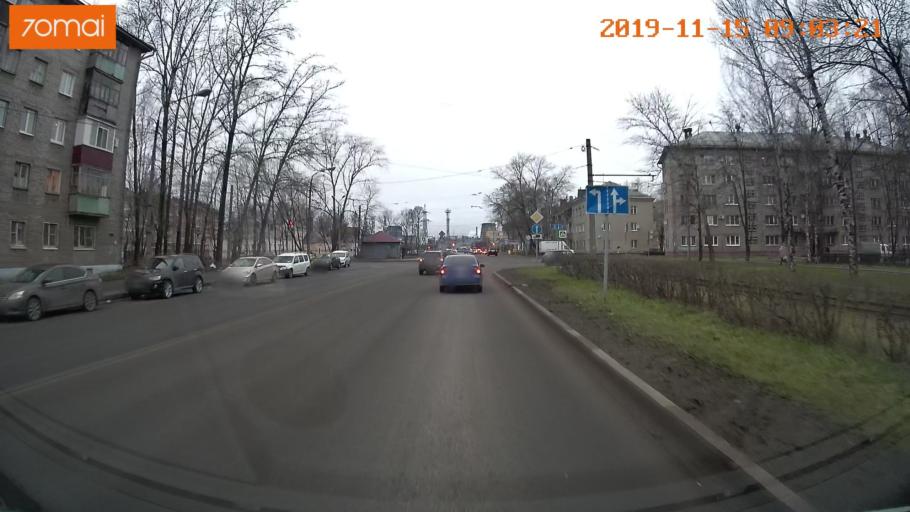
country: RU
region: Vologda
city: Cherepovets
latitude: 59.1383
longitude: 37.9222
